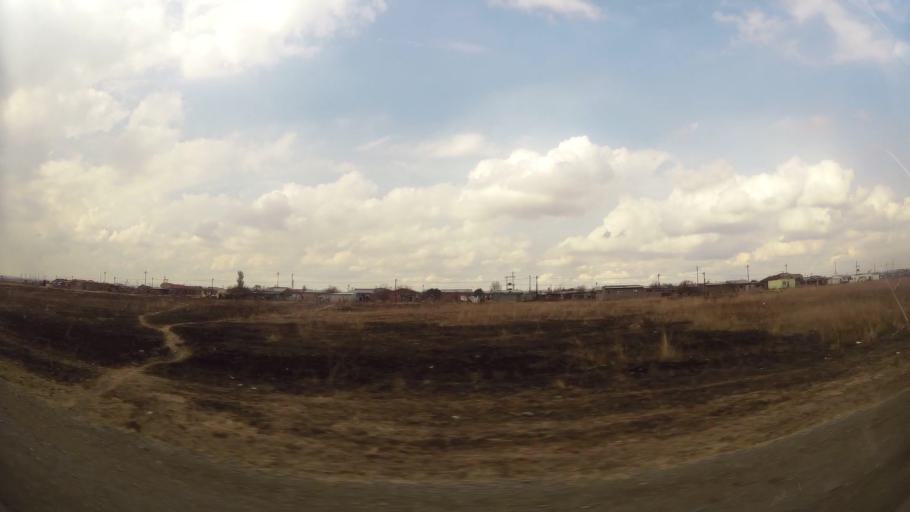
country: ZA
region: Orange Free State
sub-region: Fezile Dabi District Municipality
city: Sasolburg
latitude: -26.8506
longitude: 27.8891
